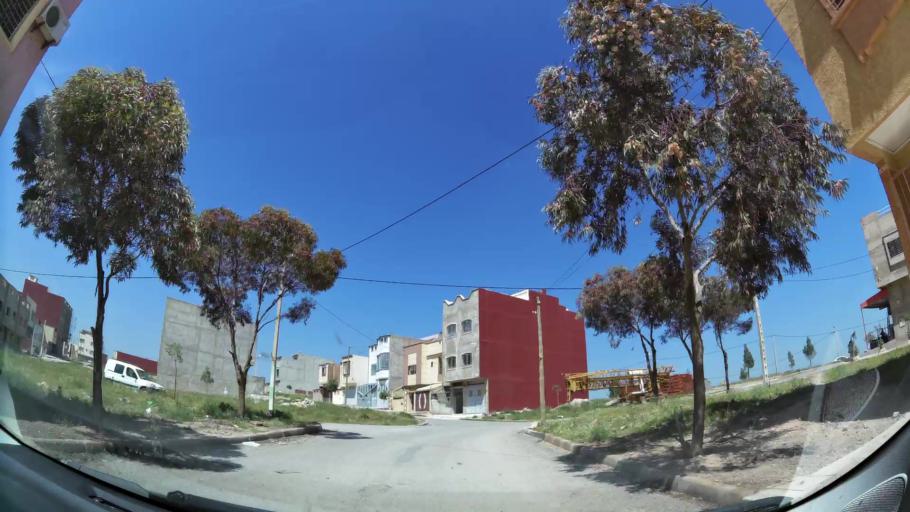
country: MA
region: Oriental
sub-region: Oujda-Angad
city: Oujda
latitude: 34.6769
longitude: -1.9444
